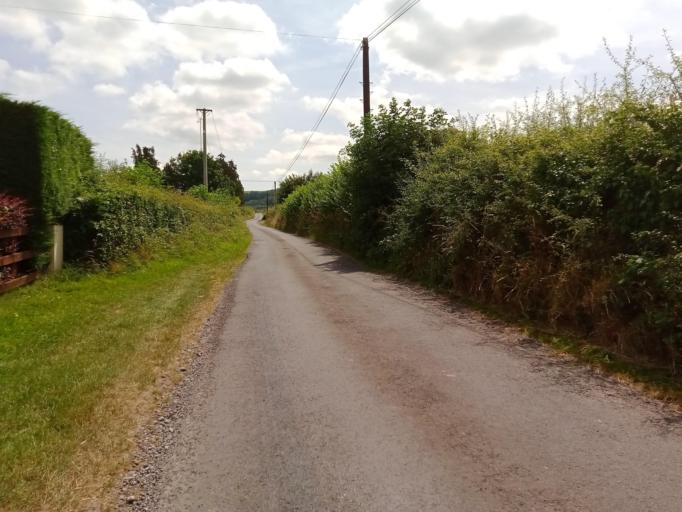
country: IE
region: Leinster
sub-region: Laois
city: Rathdowney
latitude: 52.8127
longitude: -7.4701
